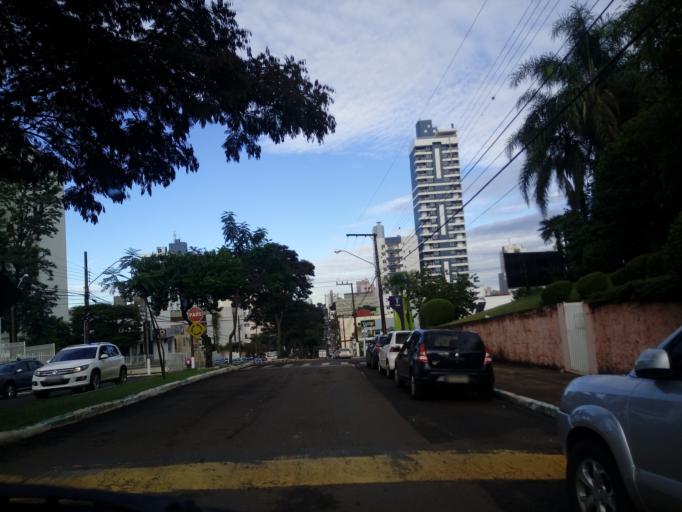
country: BR
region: Santa Catarina
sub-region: Chapeco
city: Chapeco
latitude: -27.1035
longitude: -52.6090
